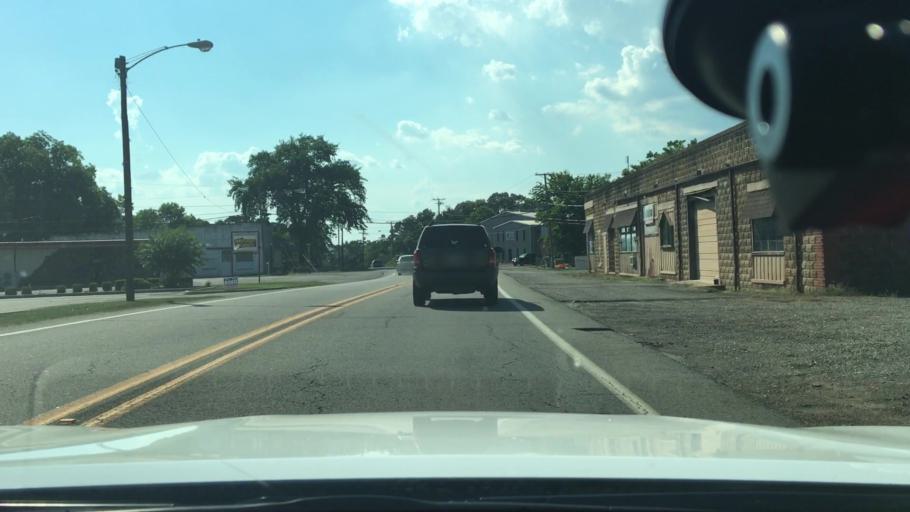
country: US
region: Arkansas
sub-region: Johnson County
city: Clarksville
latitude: 35.4720
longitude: -93.4820
